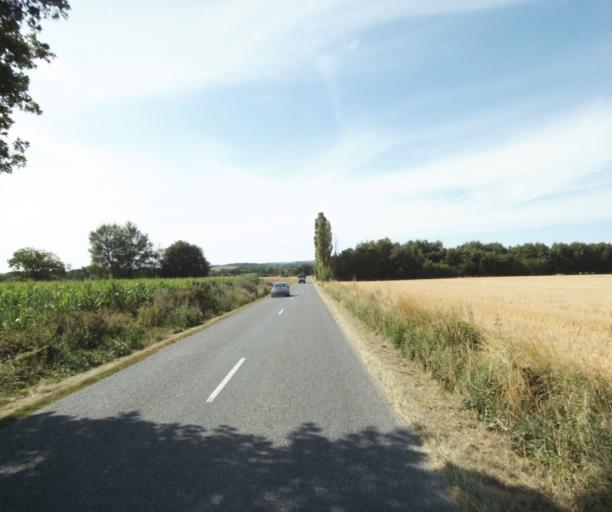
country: FR
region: Midi-Pyrenees
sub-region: Departement du Tarn
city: Soual
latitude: 43.5126
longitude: 2.0834
